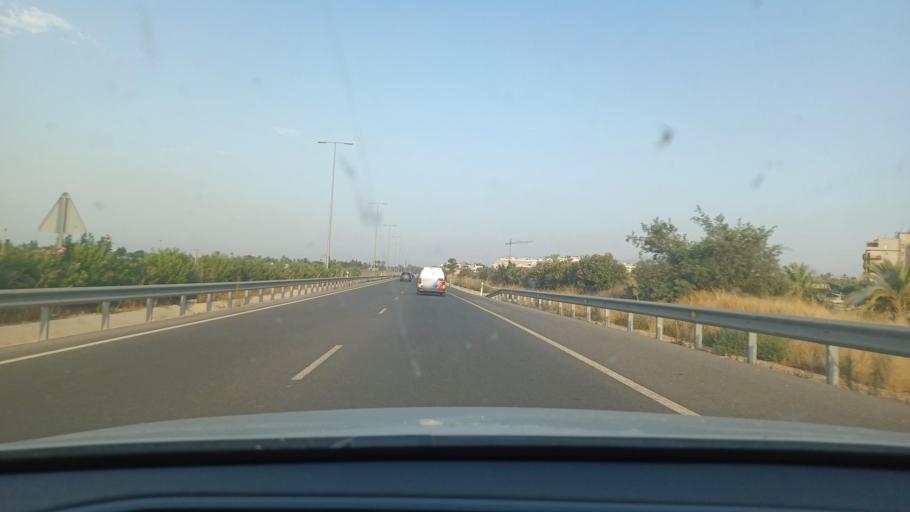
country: ES
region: Valencia
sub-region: Provincia de Alicante
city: Elche
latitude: 38.2618
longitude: -0.6617
